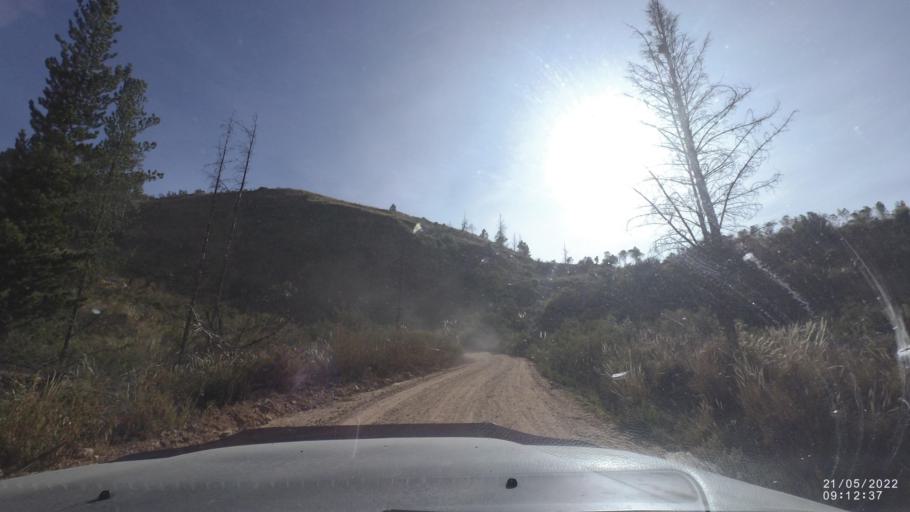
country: BO
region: Cochabamba
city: Cochabamba
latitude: -17.3680
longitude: -66.0236
